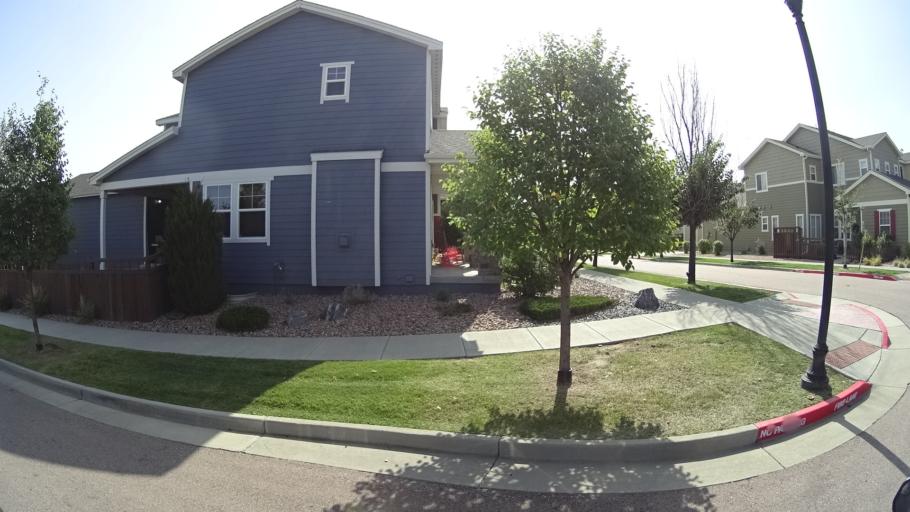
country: US
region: Colorado
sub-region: El Paso County
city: Colorado Springs
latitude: 38.8305
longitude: -104.8575
